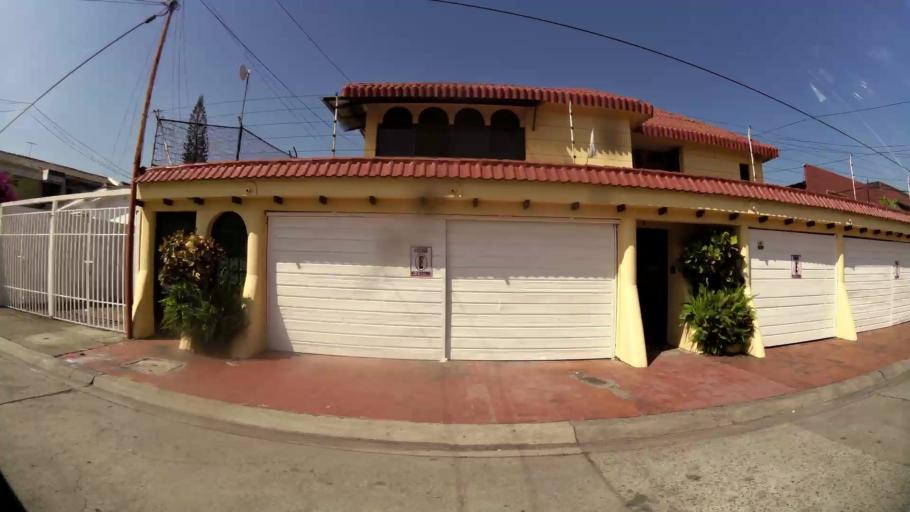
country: EC
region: Guayas
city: Guayaquil
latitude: -2.1740
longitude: -79.9088
